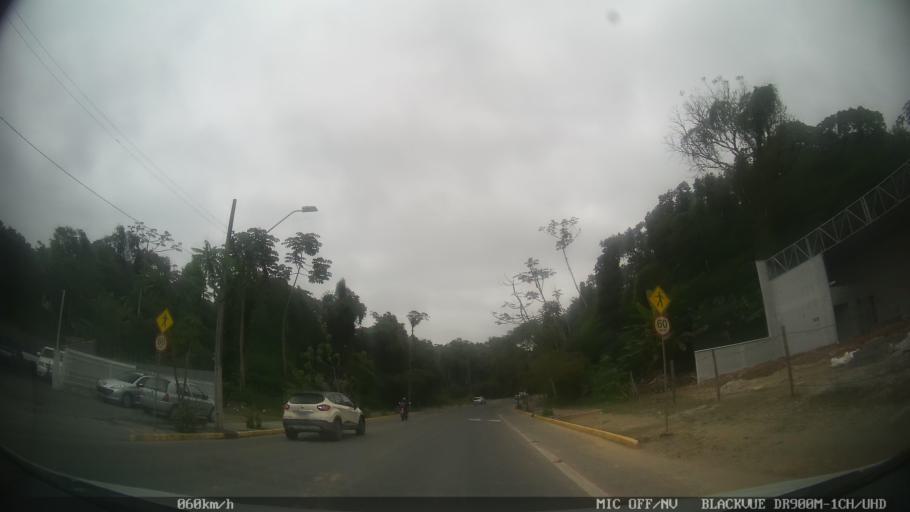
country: BR
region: Santa Catarina
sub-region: Joinville
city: Joinville
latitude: -26.3432
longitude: -48.8431
